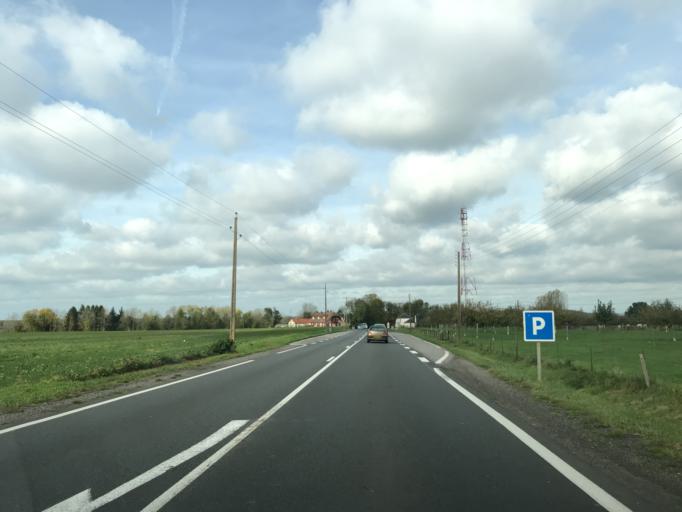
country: FR
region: Haute-Normandie
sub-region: Departement de l'Eure
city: Fleury-sur-Andelle
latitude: 49.3513
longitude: 1.3628
